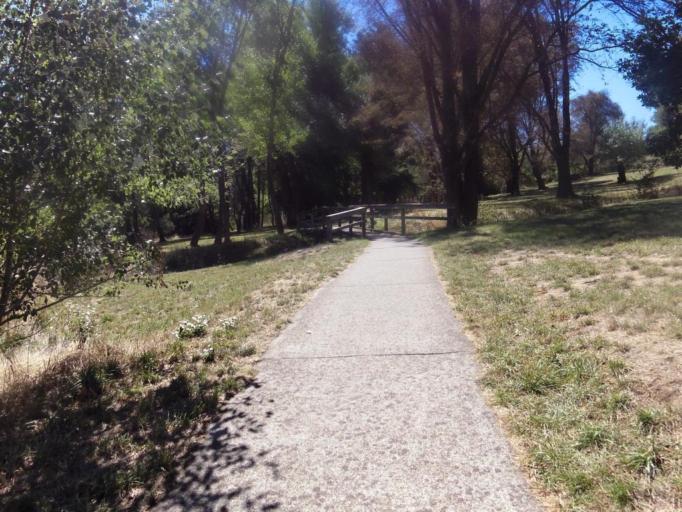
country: AU
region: Victoria
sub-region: Mount Alexander
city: Castlemaine
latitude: -37.2529
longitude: 144.4467
